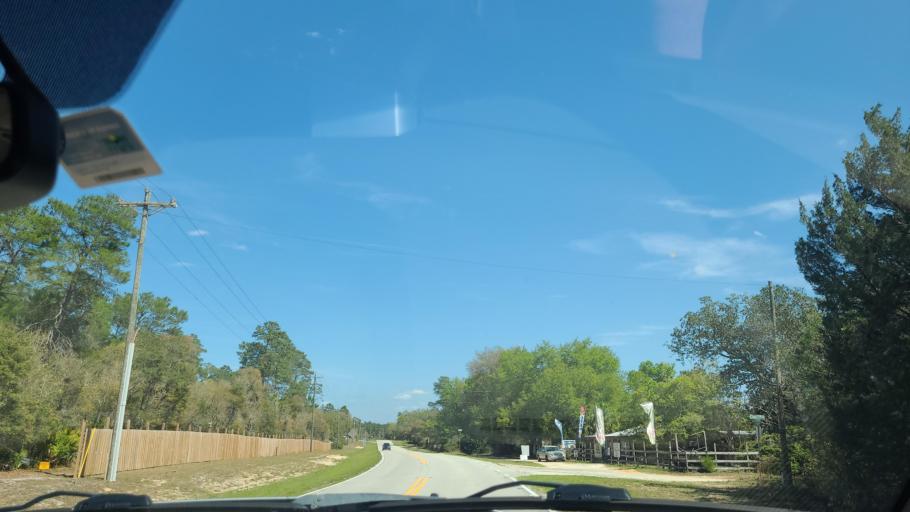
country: US
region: Florida
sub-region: Putnam County
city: Crescent City
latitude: 29.3782
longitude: -81.7658
